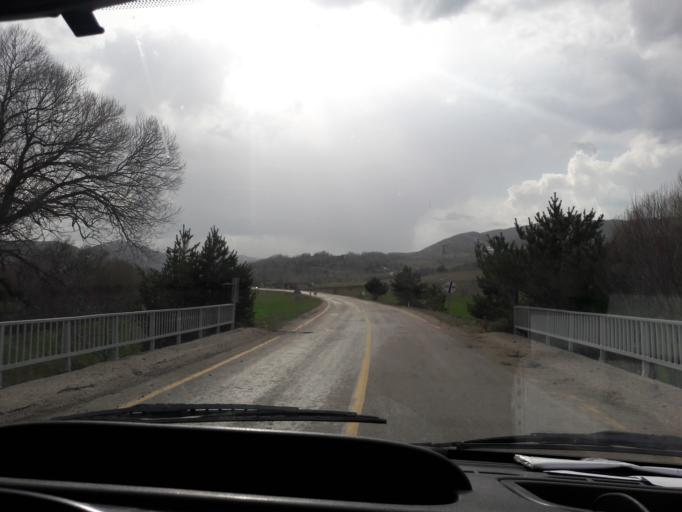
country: TR
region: Giresun
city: Alucra
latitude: 40.2670
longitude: 38.9351
